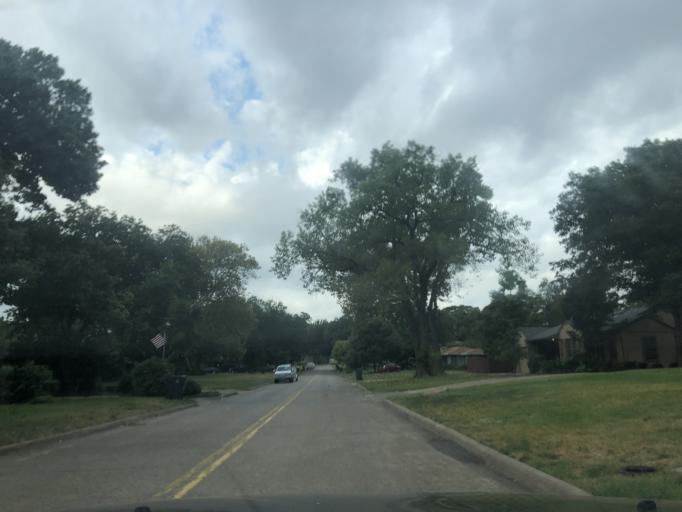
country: US
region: Texas
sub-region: Dallas County
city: Garland
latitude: 32.8880
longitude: -96.6456
